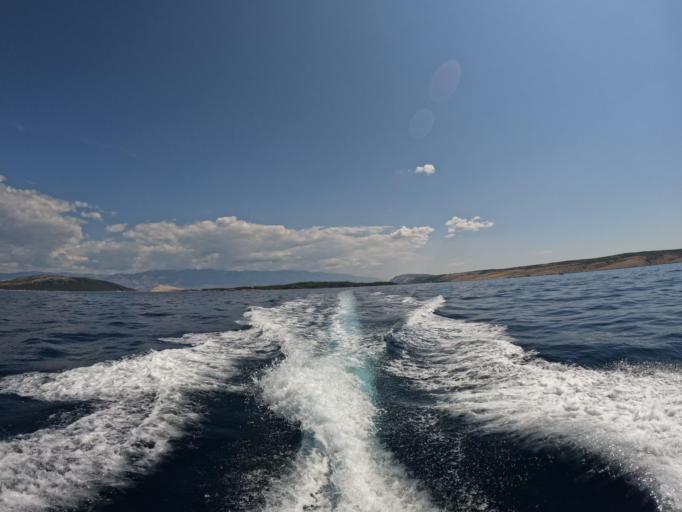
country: HR
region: Primorsko-Goranska
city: Lopar
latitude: 44.8578
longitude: 14.6992
